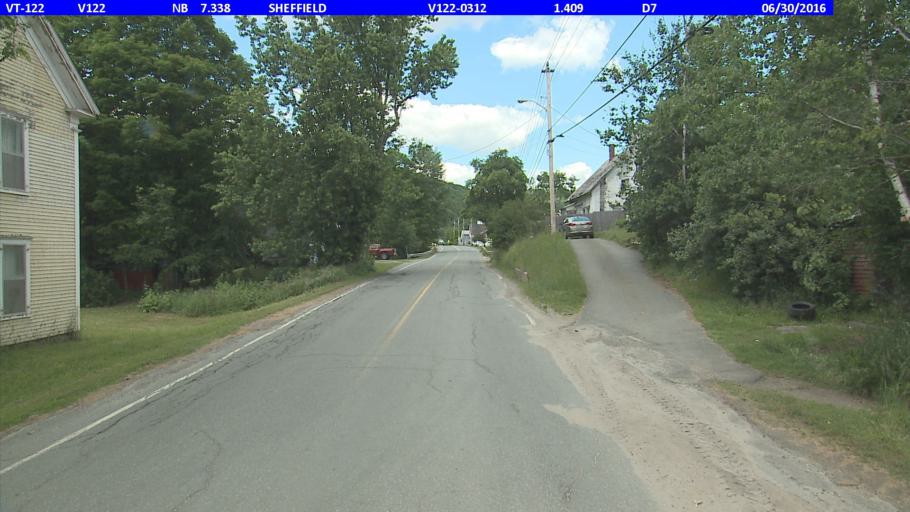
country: US
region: Vermont
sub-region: Caledonia County
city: Lyndonville
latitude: 44.6021
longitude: -72.1145
